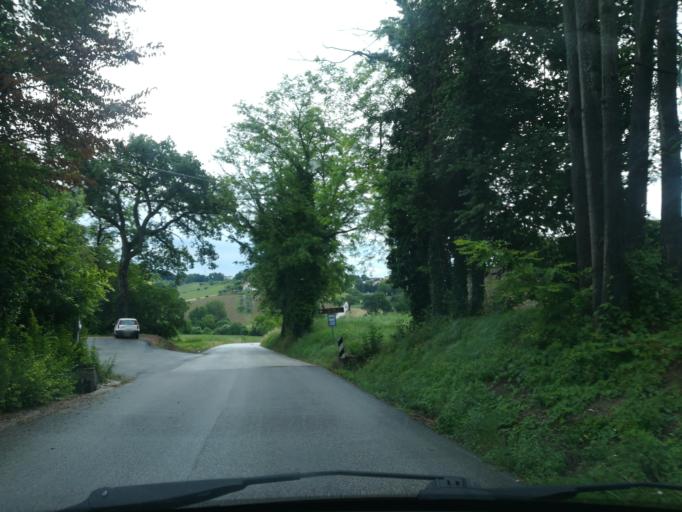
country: IT
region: The Marches
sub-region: Provincia di Macerata
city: Petriolo
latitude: 43.2251
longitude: 13.4646
